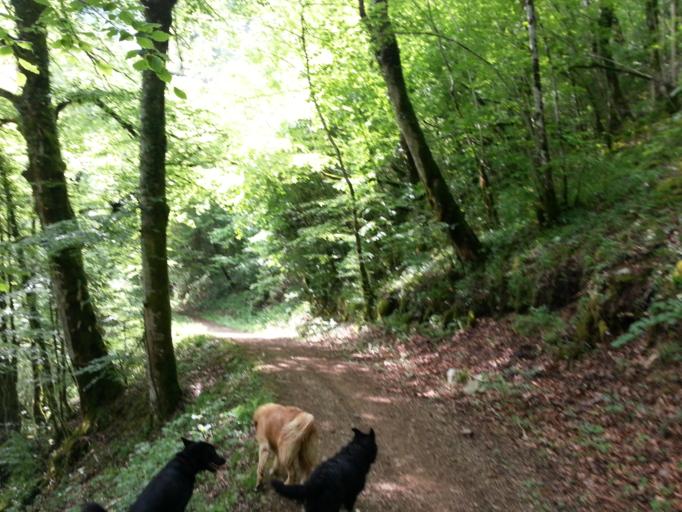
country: FR
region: Franche-Comte
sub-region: Departement du Doubs
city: Levier
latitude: 47.0026
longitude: 6.0005
